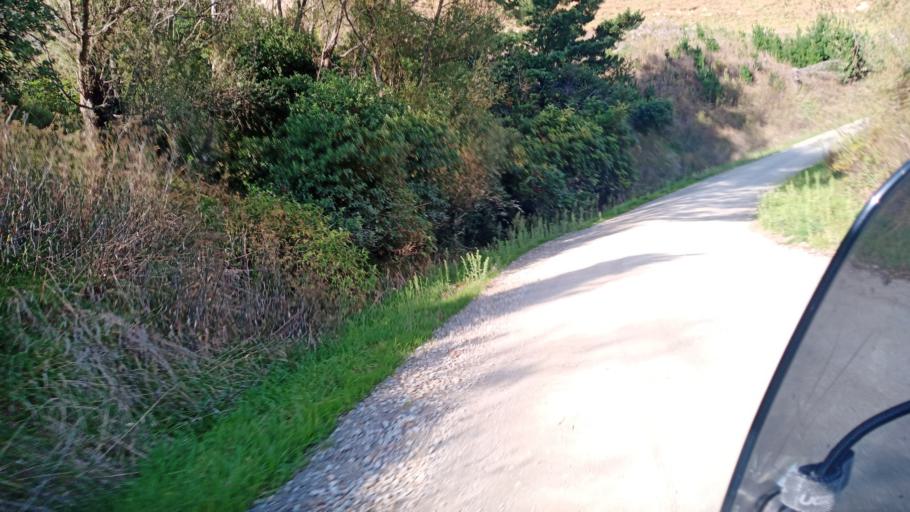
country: NZ
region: Gisborne
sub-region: Gisborne District
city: Gisborne
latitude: -38.5428
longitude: 177.5082
